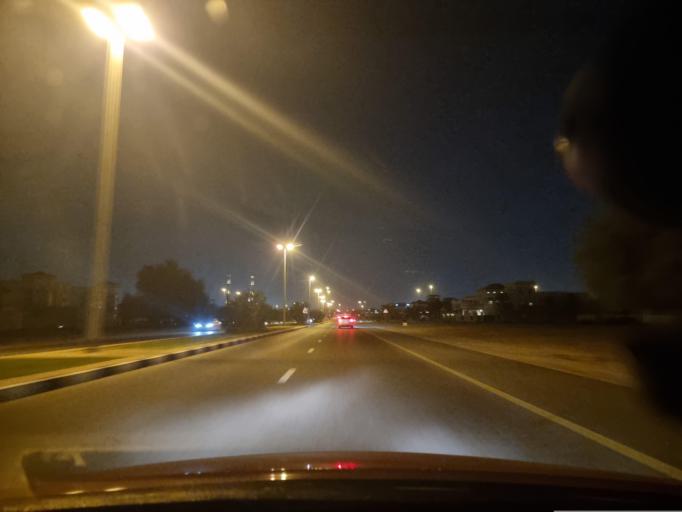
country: AE
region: Ash Shariqah
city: Sharjah
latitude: 25.3456
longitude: 55.4674
